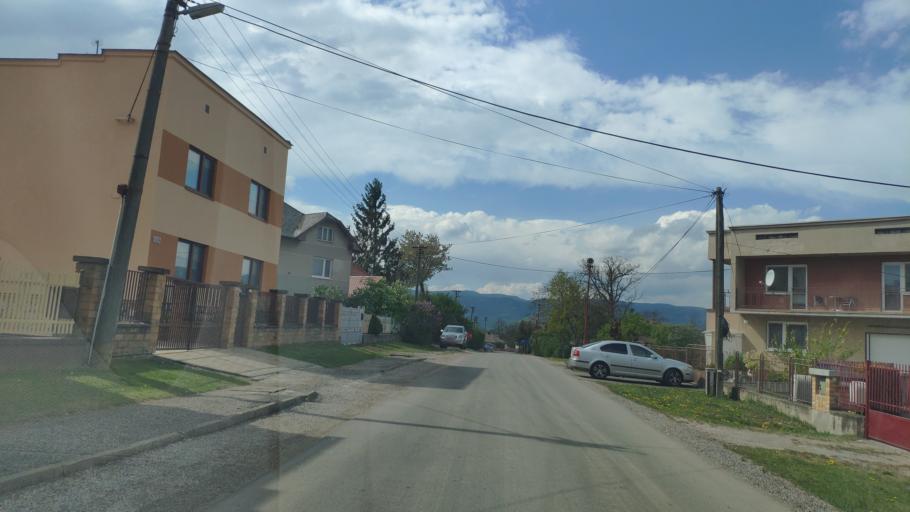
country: SK
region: Kosicky
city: Moldava nad Bodvou
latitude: 48.5808
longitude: 20.9270
